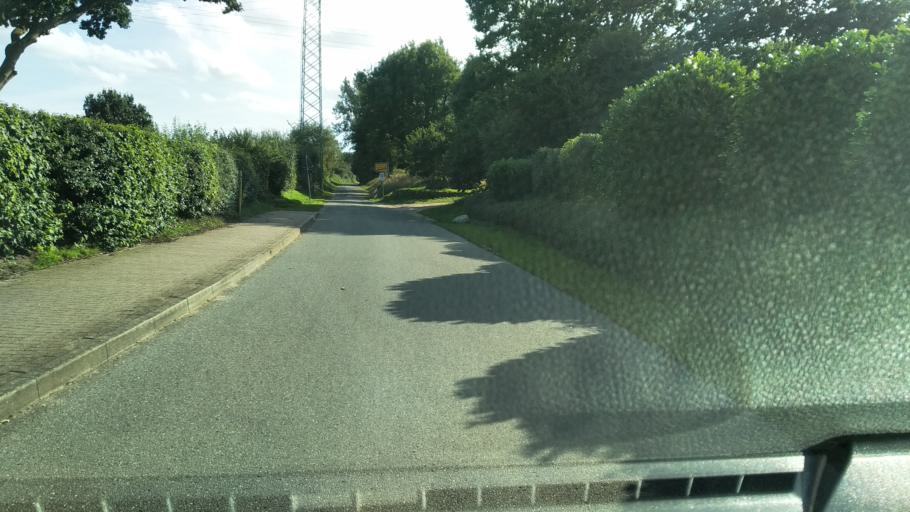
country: DE
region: Schleswig-Holstein
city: Busdorf
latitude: 54.4855
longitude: 9.5432
